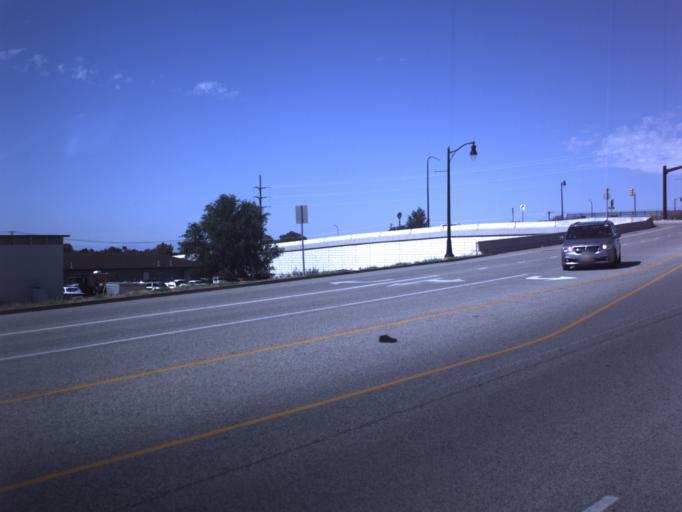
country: US
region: Utah
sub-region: Davis County
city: Layton
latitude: 41.0563
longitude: -111.9587
